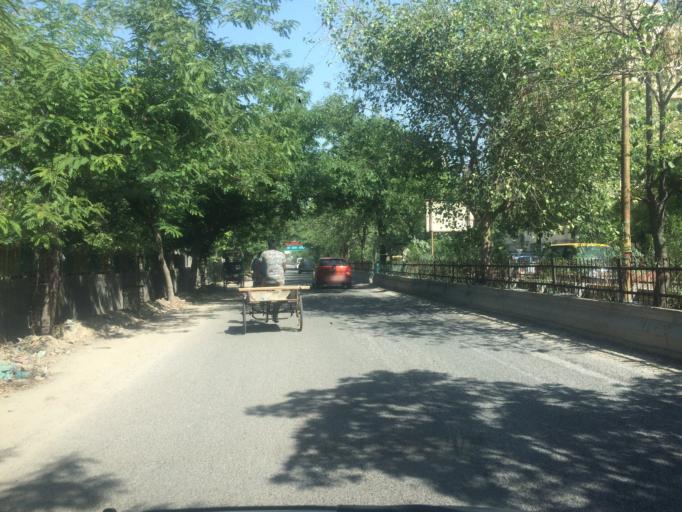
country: IN
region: Uttar Pradesh
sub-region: Gautam Buddha Nagar
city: Noida
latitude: 28.5753
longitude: 77.3692
